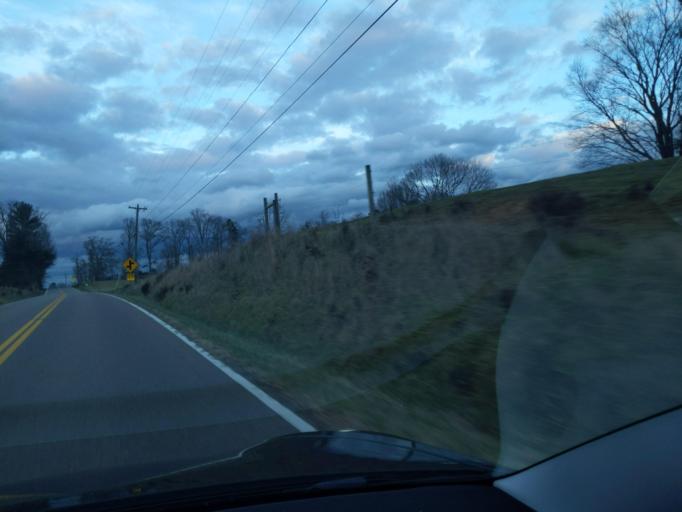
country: US
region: Tennessee
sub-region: Jefferson County
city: White Pine
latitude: 36.0879
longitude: -83.3648
